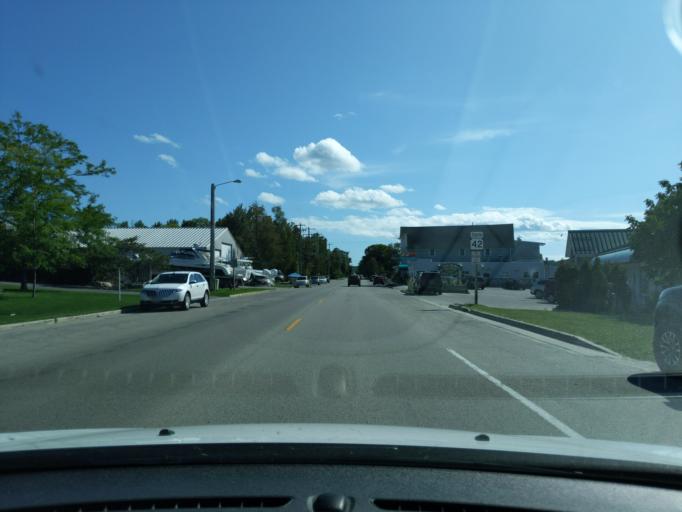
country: US
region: Wisconsin
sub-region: Door County
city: Sturgeon Bay
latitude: 45.2034
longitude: -87.1189
